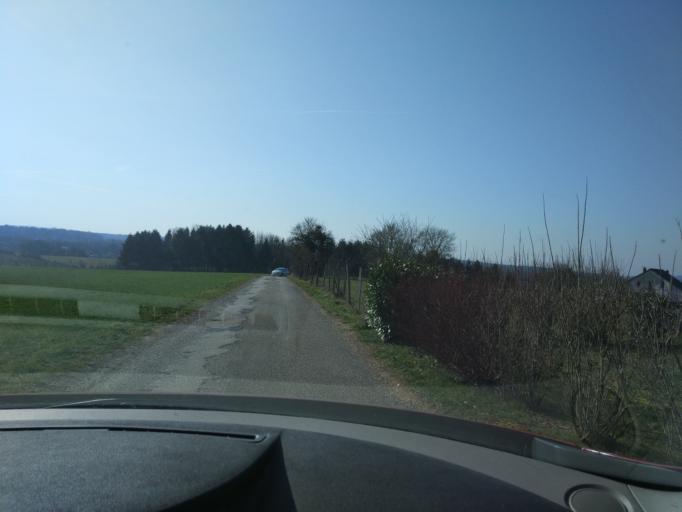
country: FR
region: Franche-Comte
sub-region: Departement du Doubs
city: Saone
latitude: 47.2156
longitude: 6.1152
